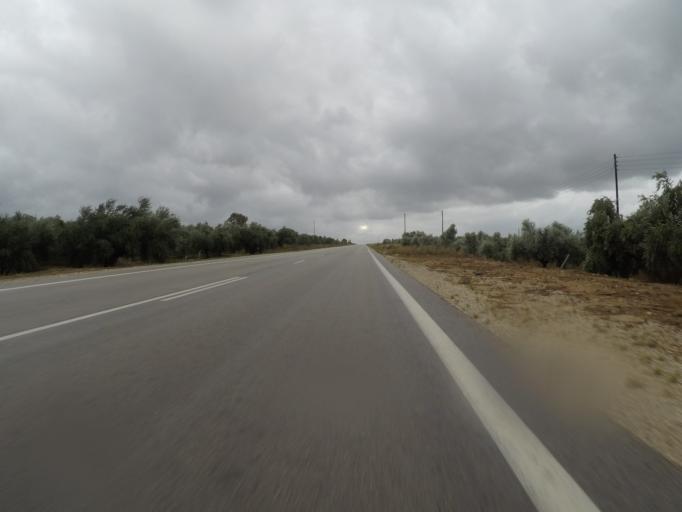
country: GR
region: Peloponnese
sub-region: Nomos Messinias
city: Gargalianoi
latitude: 37.0195
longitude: 21.6396
